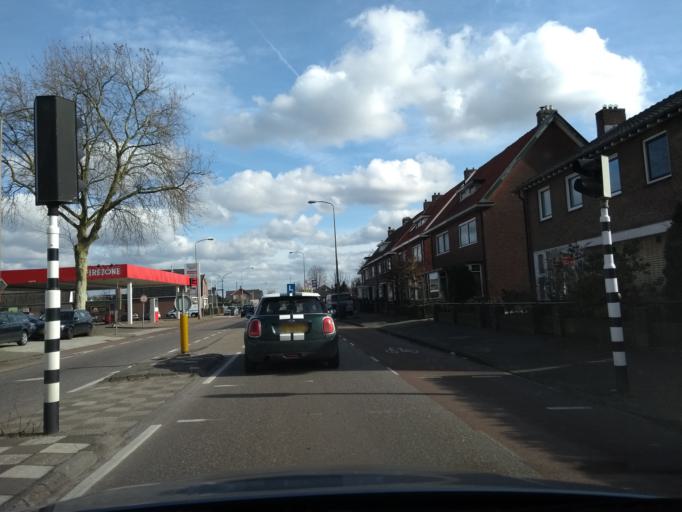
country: NL
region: Overijssel
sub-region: Gemeente Hengelo
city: Hengelo
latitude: 52.2520
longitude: 6.7881
